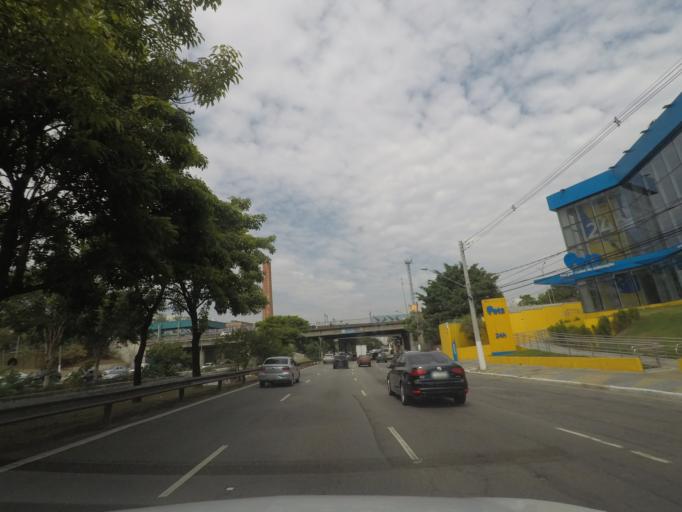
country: BR
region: Sao Paulo
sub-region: Sao Paulo
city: Sao Paulo
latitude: -23.5945
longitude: -46.6213
